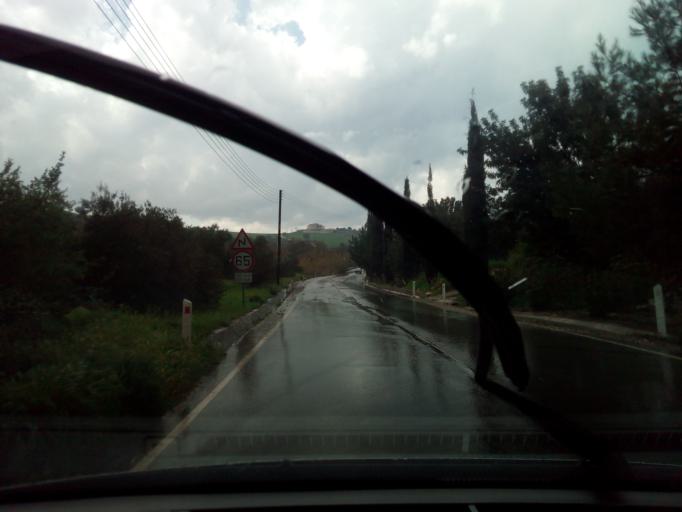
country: CY
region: Pafos
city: Polis
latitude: 35.0026
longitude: 32.4664
